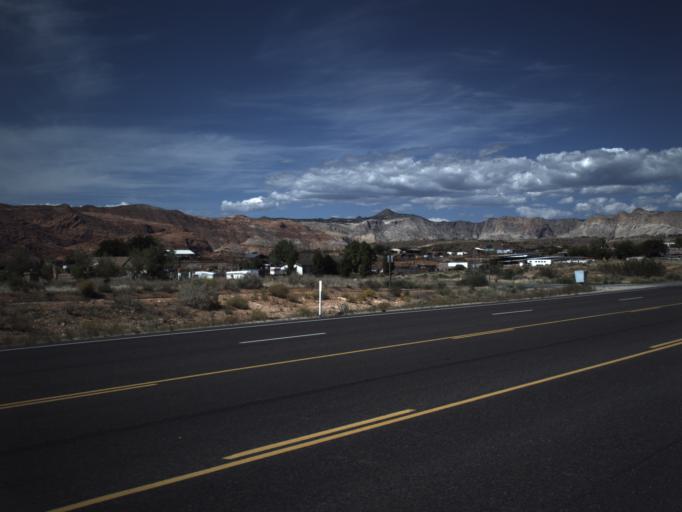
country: US
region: Utah
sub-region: Washington County
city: Santa Clara
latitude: 37.1805
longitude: -113.6190
